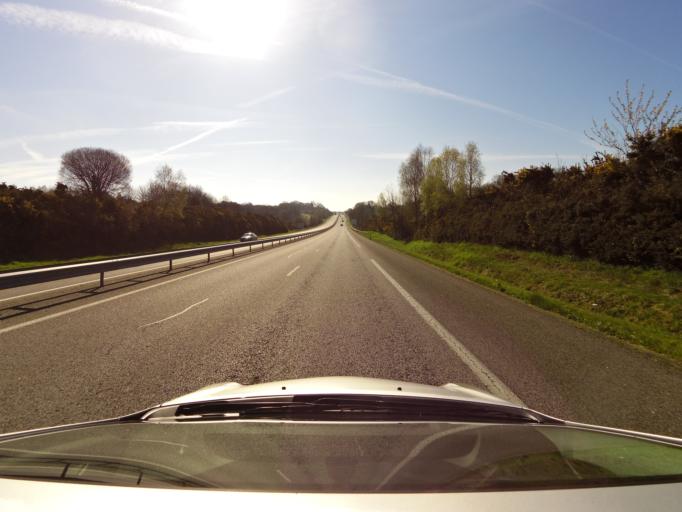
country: FR
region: Brittany
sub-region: Departement du Morbihan
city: Augan
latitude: 47.9337
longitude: -2.2521
